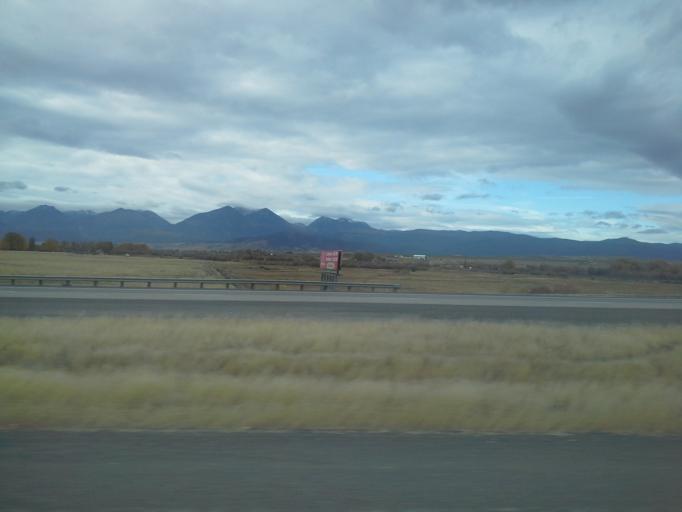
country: US
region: Oregon
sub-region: Union County
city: Union
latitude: 45.0207
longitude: -117.9233
